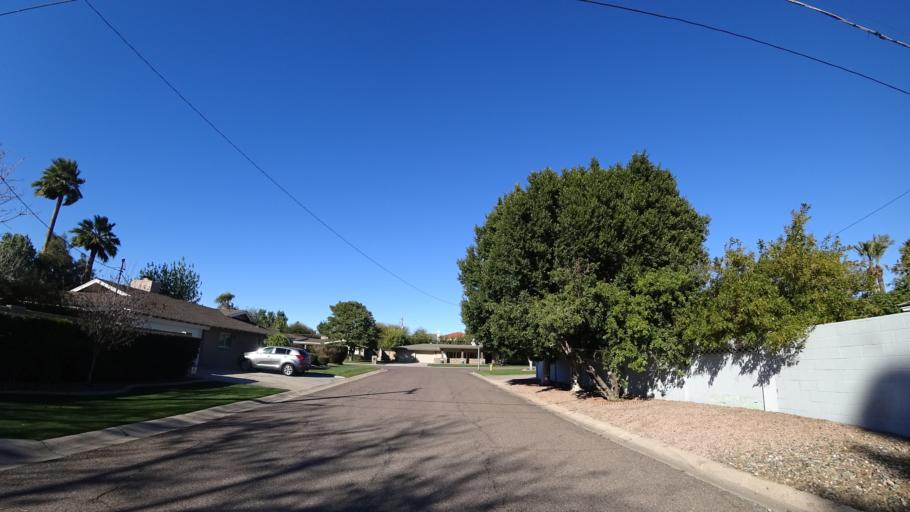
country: US
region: Arizona
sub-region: Maricopa County
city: Phoenix
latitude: 33.5473
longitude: -112.0715
